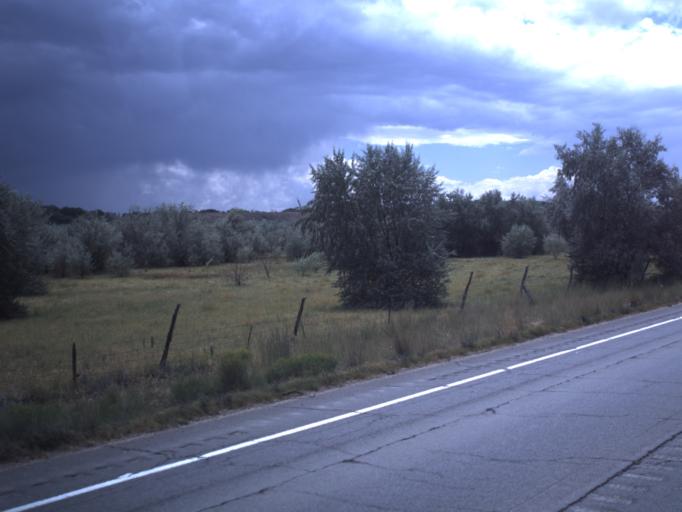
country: US
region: Utah
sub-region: Duchesne County
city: Roosevelt
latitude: 40.1818
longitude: -110.1074
